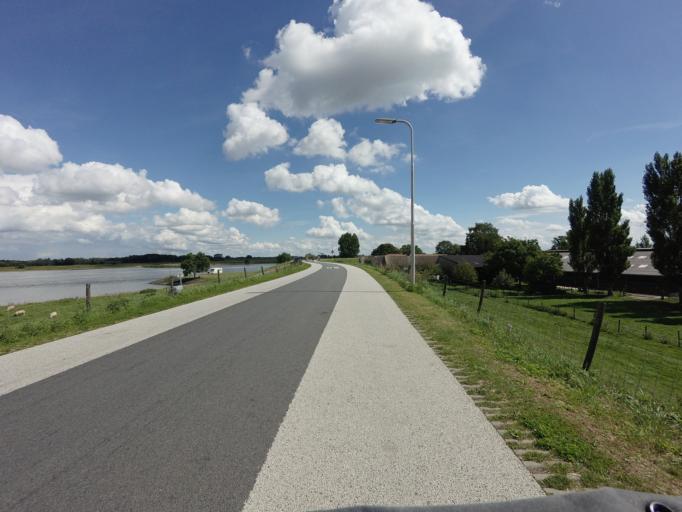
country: NL
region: Utrecht
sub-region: Gemeente IJsselstein
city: IJsselstein
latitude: 51.9738
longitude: 5.0092
